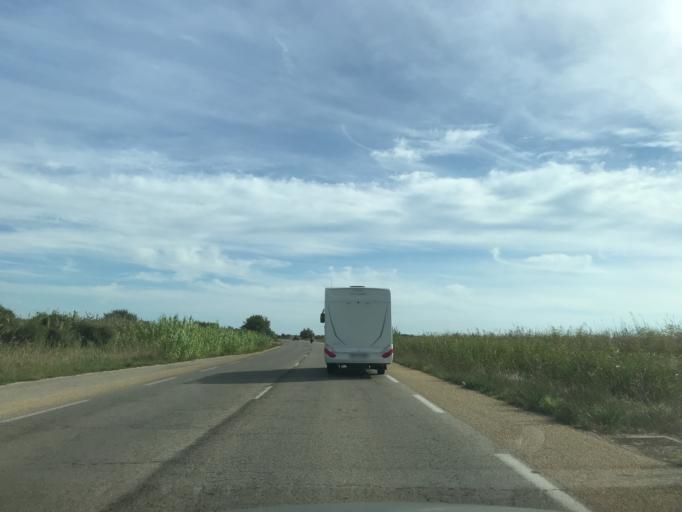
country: FR
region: Provence-Alpes-Cote d'Azur
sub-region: Departement des Bouches-du-Rhone
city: Saintes-Maries-de-la-Mer
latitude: 43.5123
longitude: 4.3986
